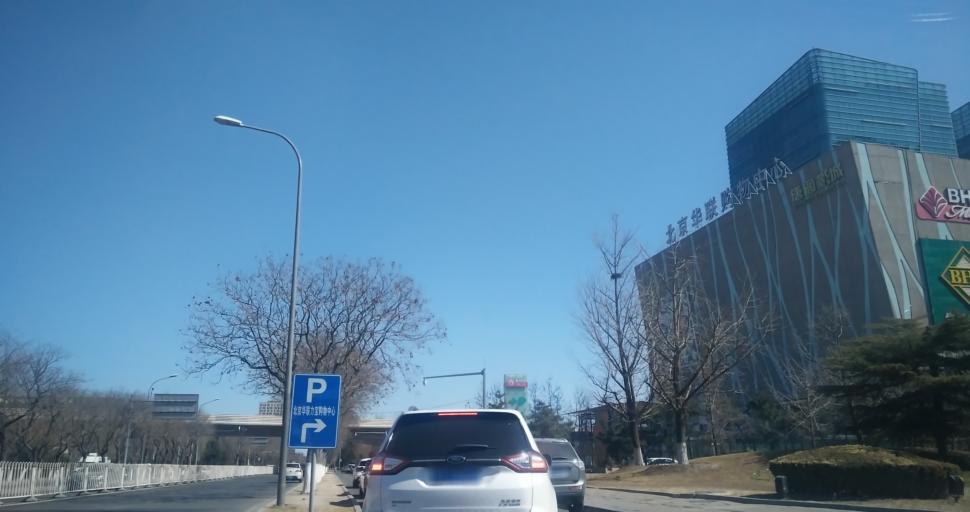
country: CN
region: Beijing
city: Jiugong
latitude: 39.8048
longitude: 116.4944
